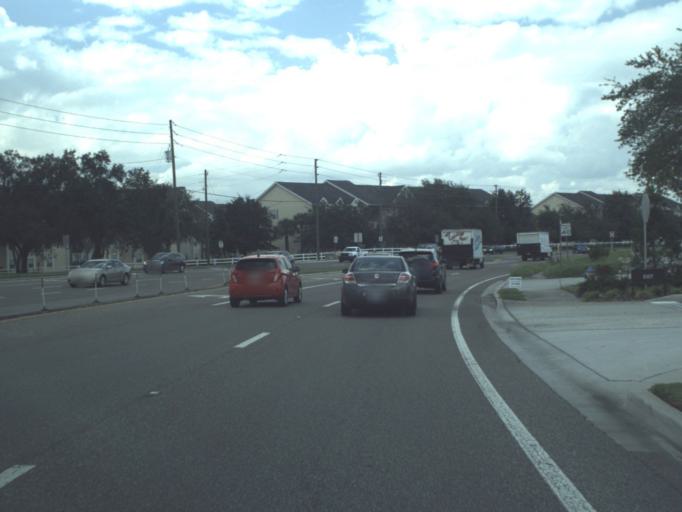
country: US
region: Florida
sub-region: Pasco County
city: Elfers
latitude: 28.2178
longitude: -82.6926
